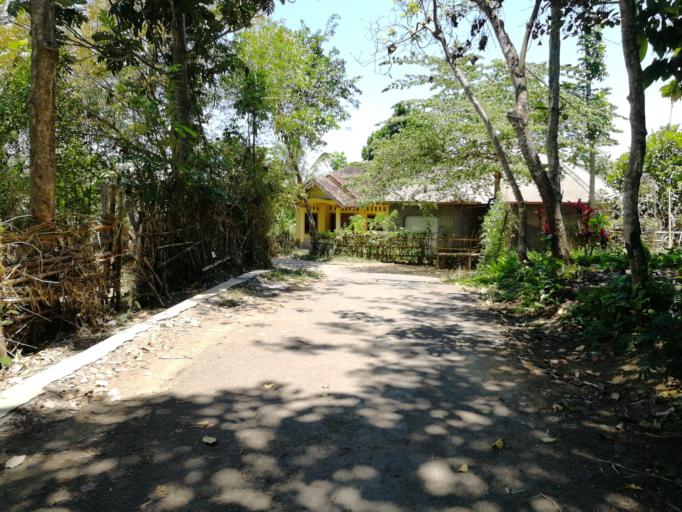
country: ID
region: West Nusa Tenggara
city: Tetebatu
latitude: -8.5485
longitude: 116.4195
